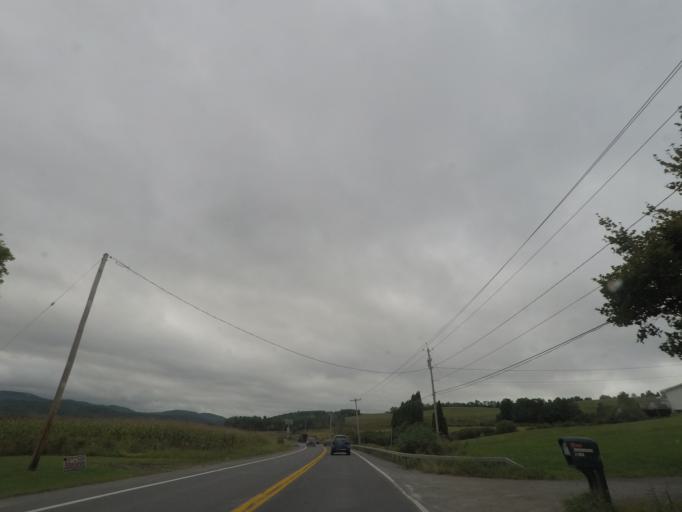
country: US
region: New York
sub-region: Rensselaer County
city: Hoosick Falls
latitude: 42.8732
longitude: -73.3544
